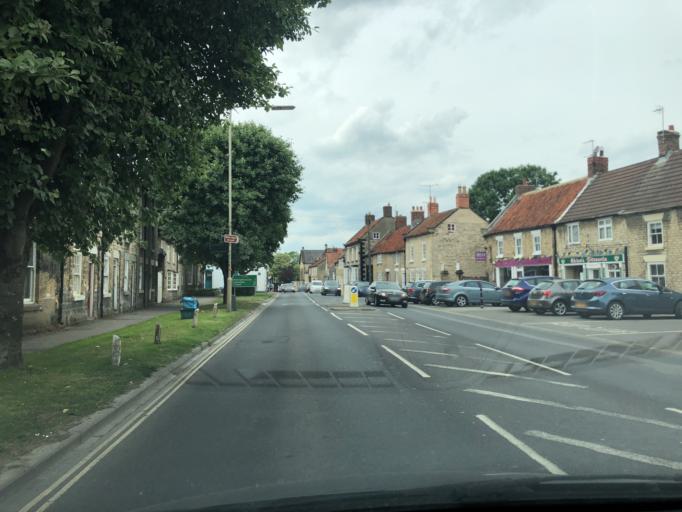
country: GB
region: England
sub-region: North Yorkshire
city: Pickering
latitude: 54.2444
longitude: -0.7760
